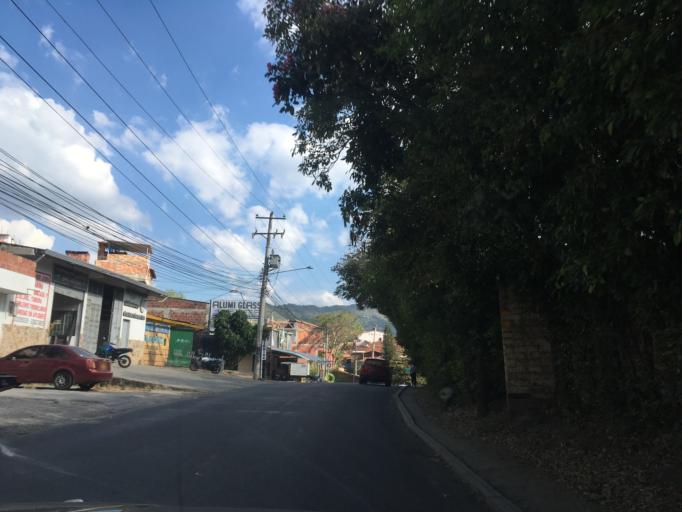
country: CO
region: Santander
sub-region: San Gil
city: San Gil
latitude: 6.5614
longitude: -73.1407
